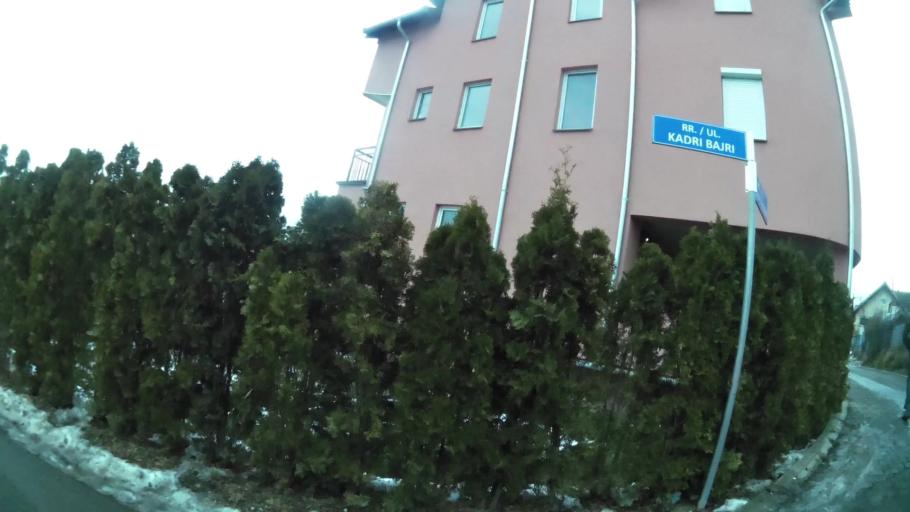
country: XK
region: Pristina
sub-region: Komuna e Prishtines
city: Pristina
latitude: 42.6401
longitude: 21.1653
